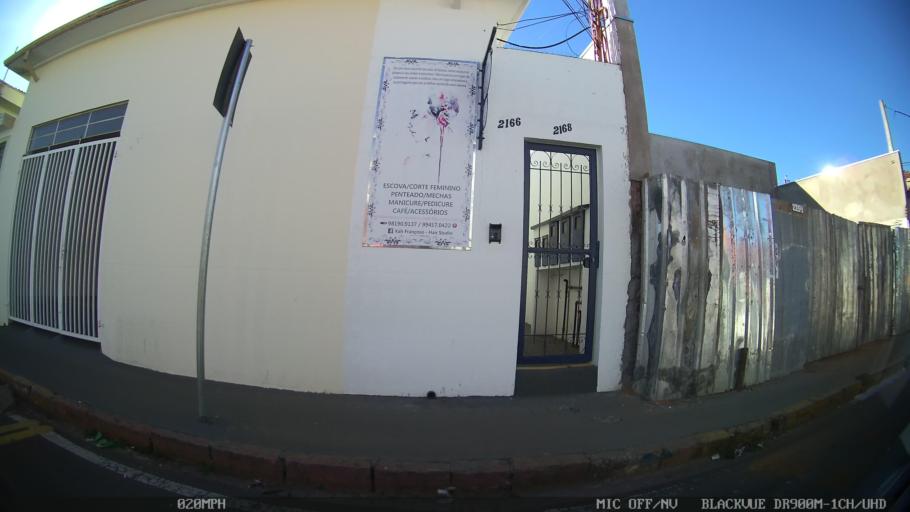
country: BR
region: Sao Paulo
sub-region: Franca
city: Franca
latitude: -20.5342
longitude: -47.4020
